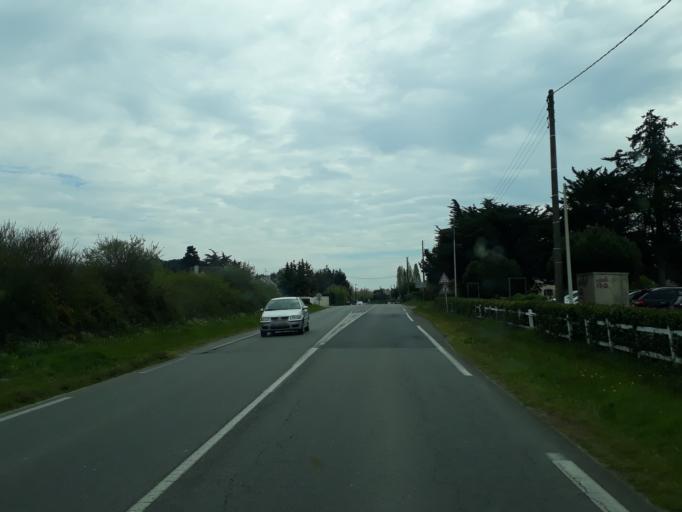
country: FR
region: Pays de la Loire
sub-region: Departement de la Loire-Atlantique
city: Guerande
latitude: 47.2999
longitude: -2.4076
